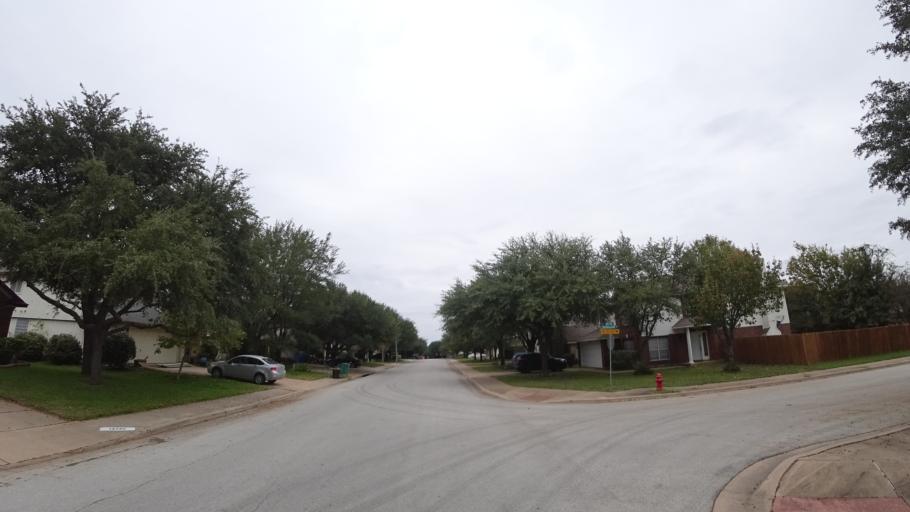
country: US
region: Texas
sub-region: Travis County
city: Wells Branch
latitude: 30.4484
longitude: -97.6876
